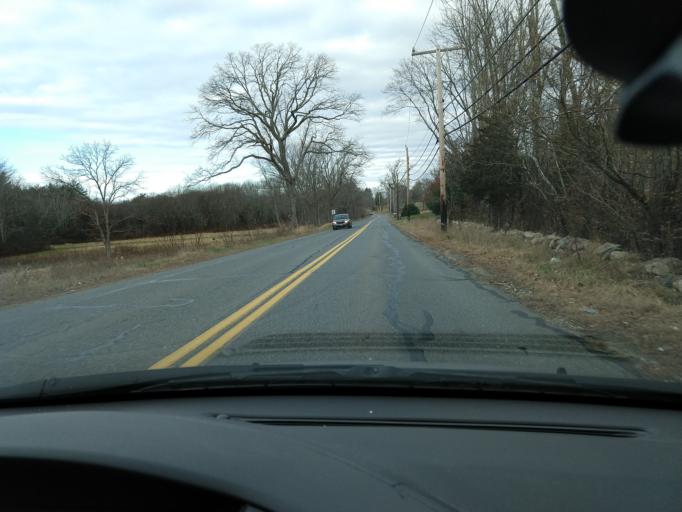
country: US
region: Massachusetts
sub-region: Middlesex County
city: Lincoln
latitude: 42.4555
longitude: -71.3147
